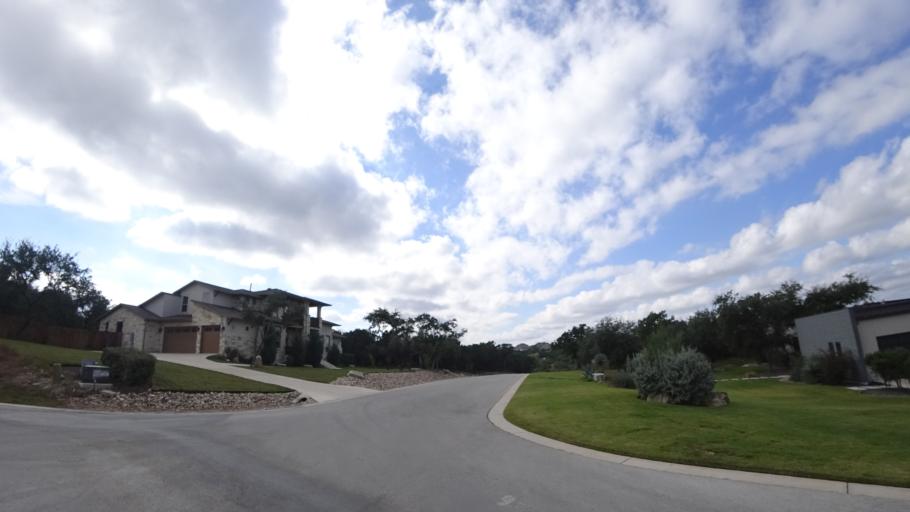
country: US
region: Texas
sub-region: Travis County
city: Bee Cave
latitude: 30.2563
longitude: -97.9270
